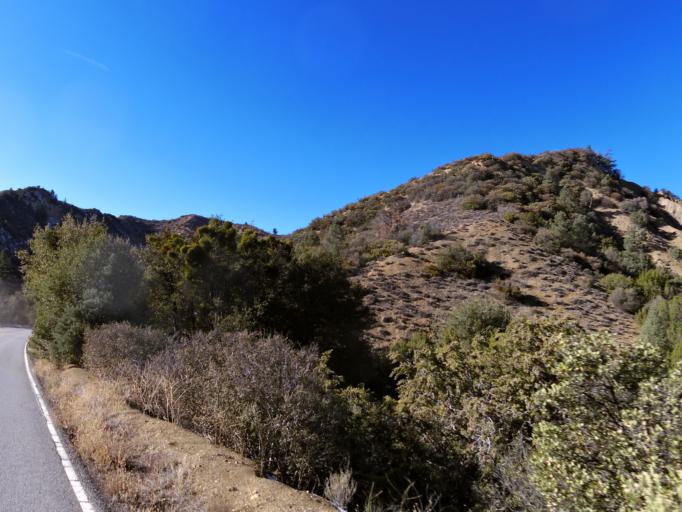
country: US
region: California
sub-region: Ventura County
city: Meiners Oaks
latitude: 34.6694
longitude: -119.3689
